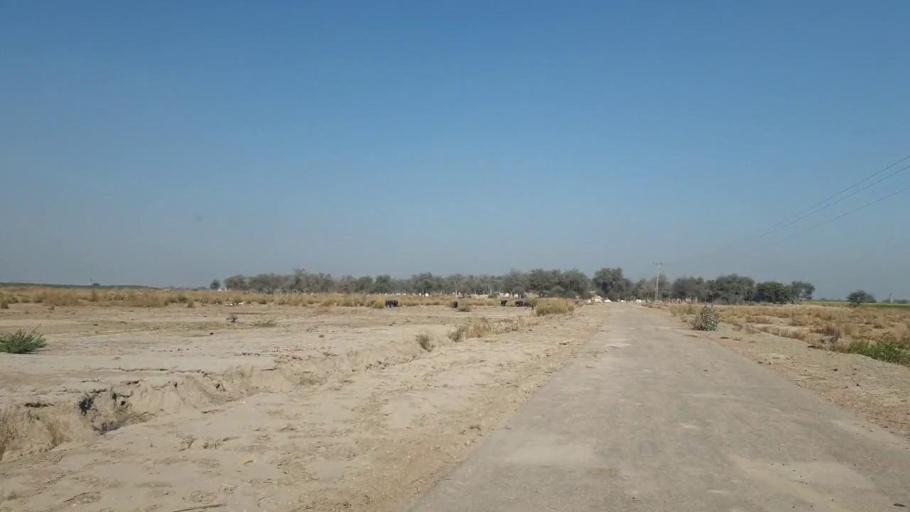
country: PK
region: Sindh
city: Shahpur Chakar
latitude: 26.1227
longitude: 68.6047
